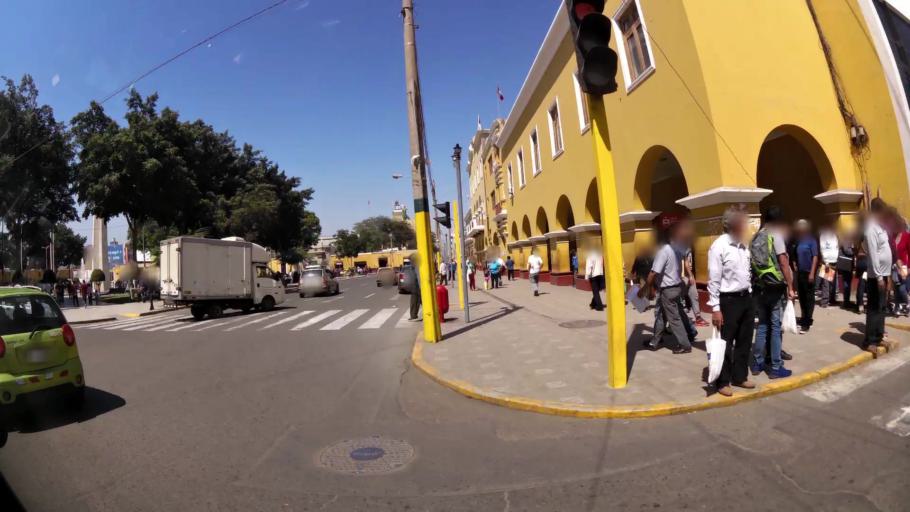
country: PE
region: Ica
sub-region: Provincia de Ica
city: Ica
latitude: -14.0637
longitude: -75.7297
